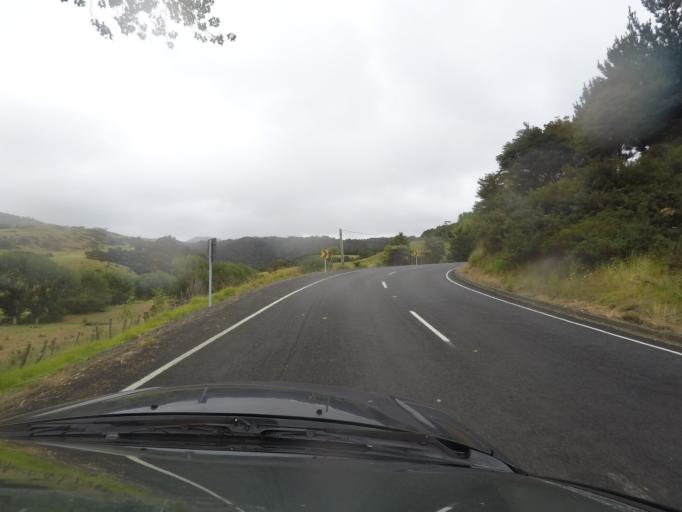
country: NZ
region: Auckland
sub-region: Auckland
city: Warkworth
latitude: -36.2718
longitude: 174.6985
